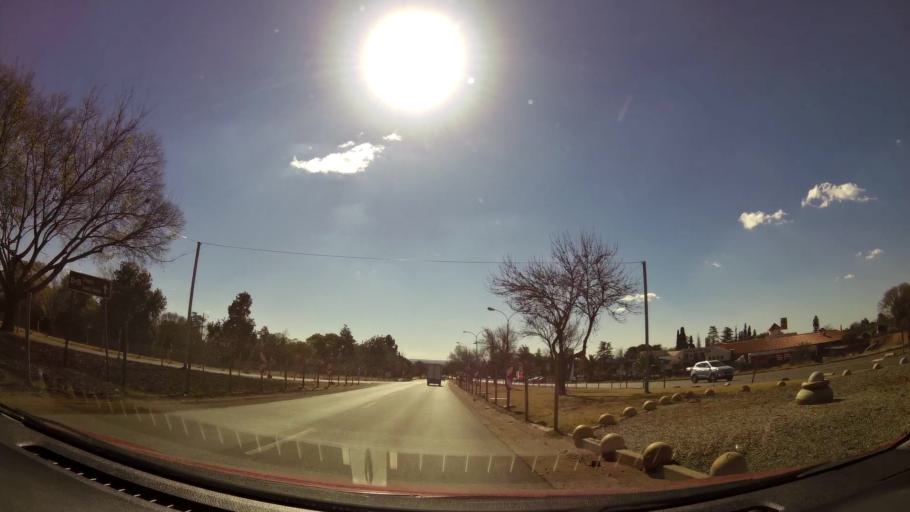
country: ZA
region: Gauteng
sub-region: West Rand District Municipality
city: Carletonville
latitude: -26.3740
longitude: 27.4063
